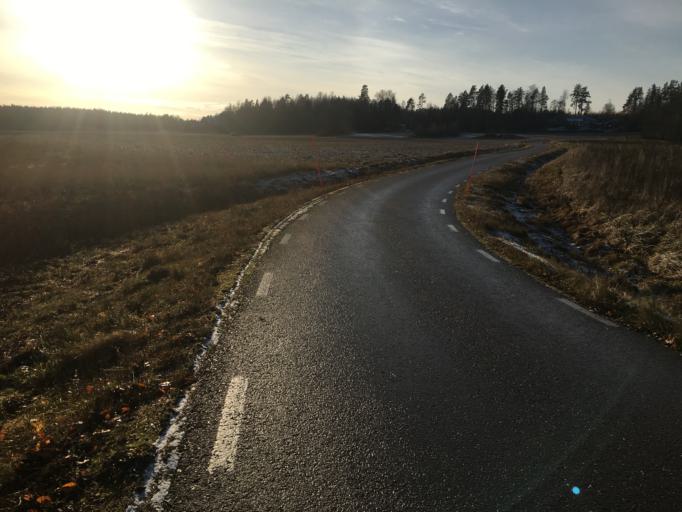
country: SE
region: Vaestmanland
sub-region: Vasteras
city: Vasteras
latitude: 59.6440
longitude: 16.4796
